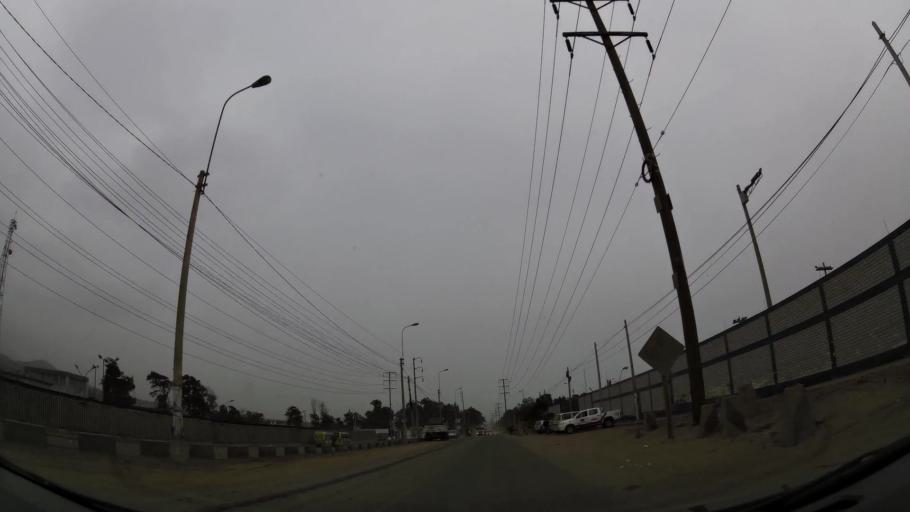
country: PE
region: Lima
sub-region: Lima
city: Surco
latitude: -12.1783
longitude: -76.9753
